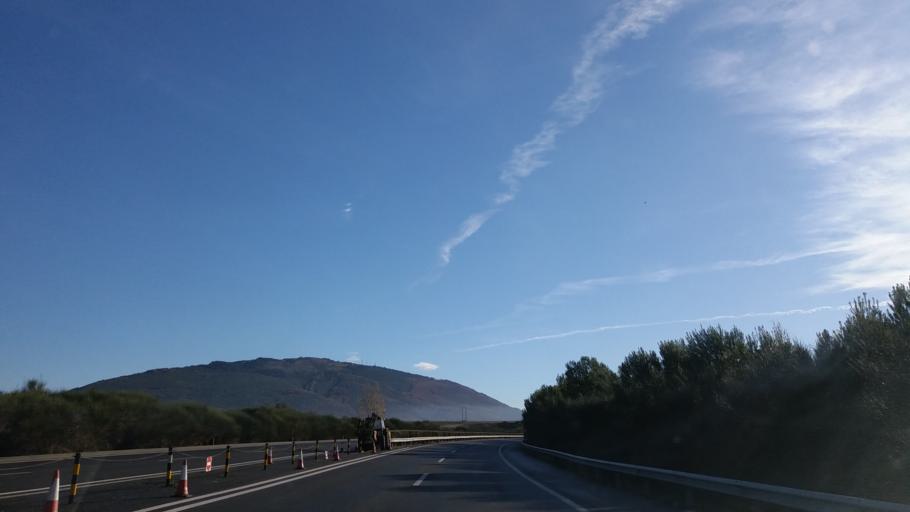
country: ES
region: Navarre
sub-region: Provincia de Navarra
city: Berriobeiti
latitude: 42.8539
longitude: -1.7170
